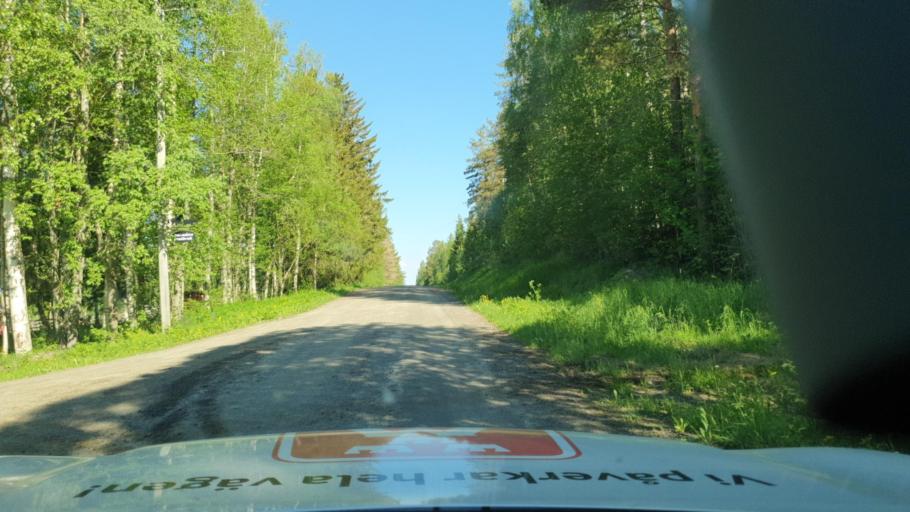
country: SE
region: Vaesterbotten
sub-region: Vannas Kommun
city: Vannasby
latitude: 64.0124
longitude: 19.7701
